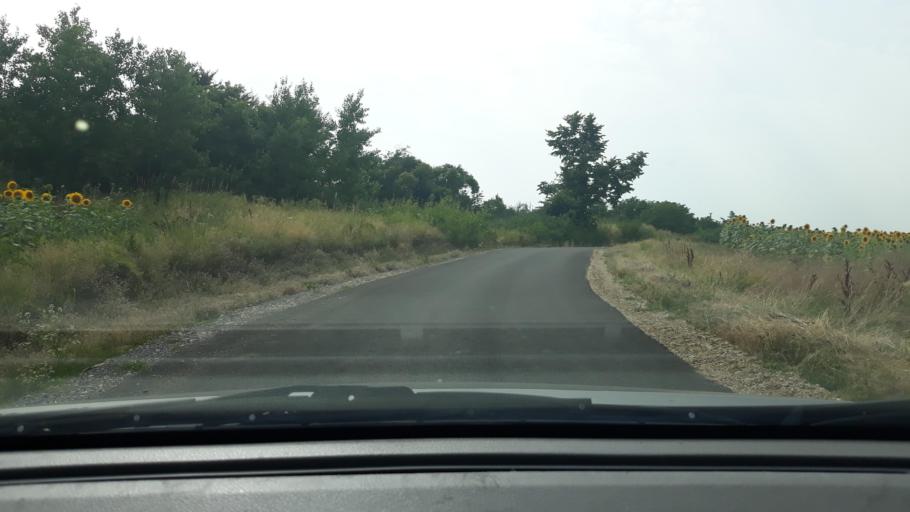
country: RO
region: Bihor
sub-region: Comuna Chislaz
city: Misca
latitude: 47.2611
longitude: 22.2944
